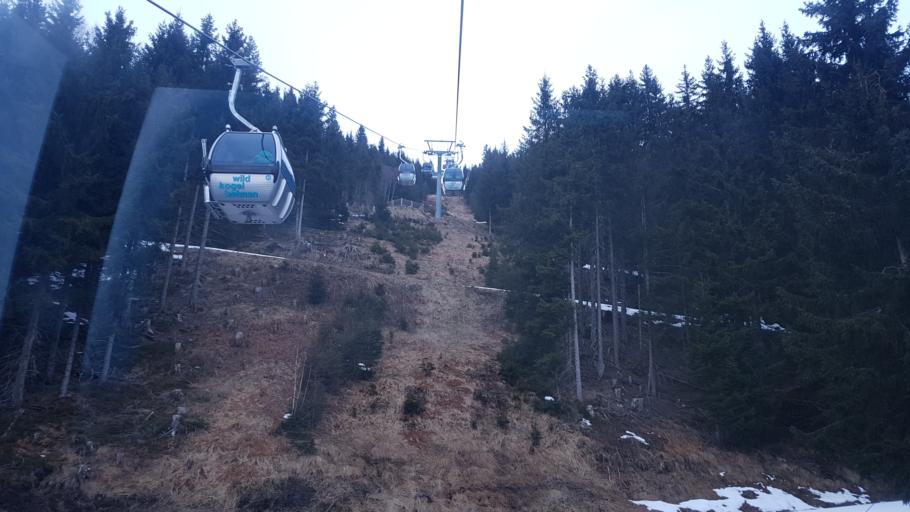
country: AT
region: Salzburg
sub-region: Politischer Bezirk Zell am See
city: Neukirchen am Grossvenediger
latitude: 47.2666
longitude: 12.2810
